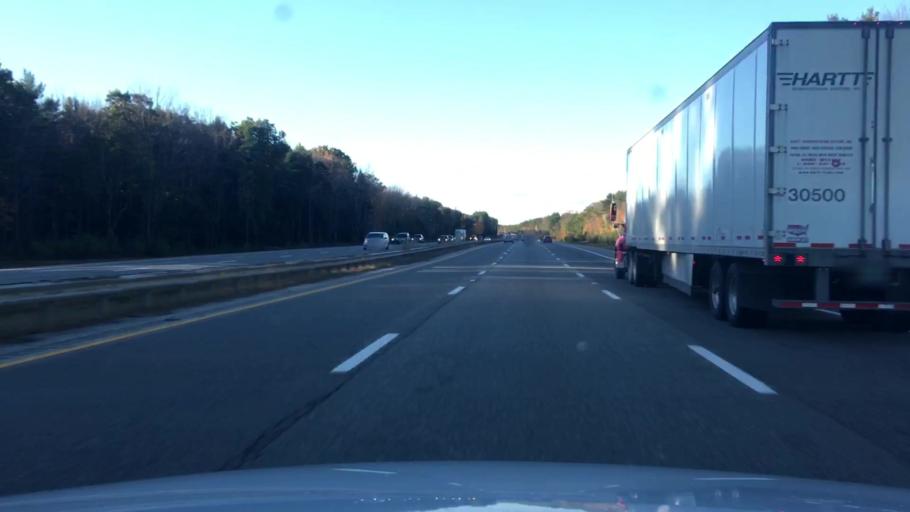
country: US
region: Maine
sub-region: York County
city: West Kennebunk
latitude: 43.4358
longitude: -70.5434
